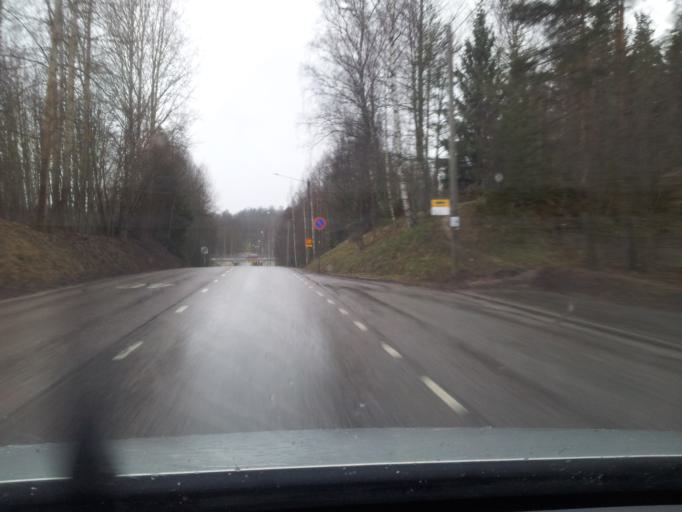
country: FI
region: Uusimaa
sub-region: Helsinki
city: Espoo
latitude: 60.1961
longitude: 24.5890
